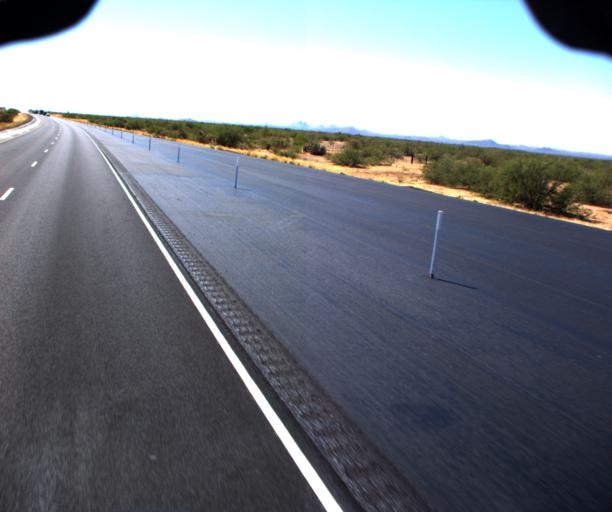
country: US
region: Arizona
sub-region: Yavapai County
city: Congress
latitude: 34.1009
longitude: -112.9185
